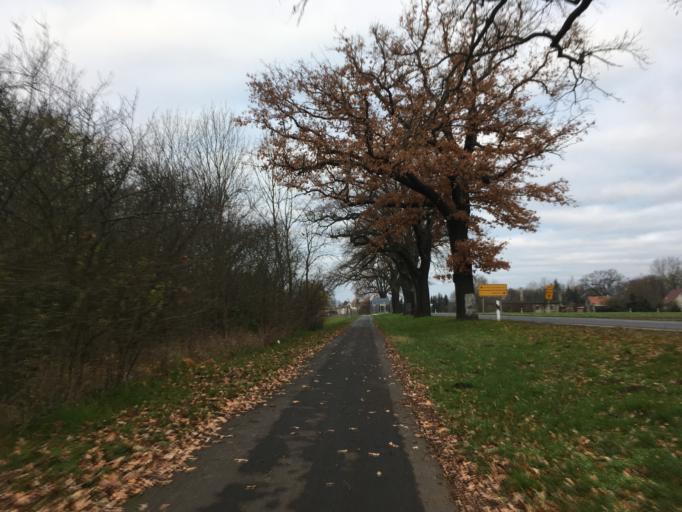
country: DE
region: Brandenburg
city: Seelow
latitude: 52.5798
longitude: 14.3397
